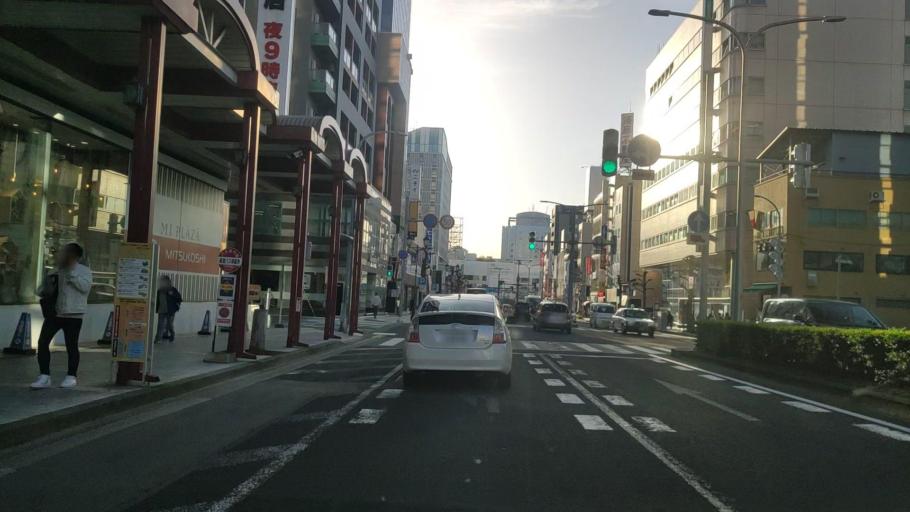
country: JP
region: Yamagata
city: Yamagata-shi
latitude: 38.2469
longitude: 140.3318
